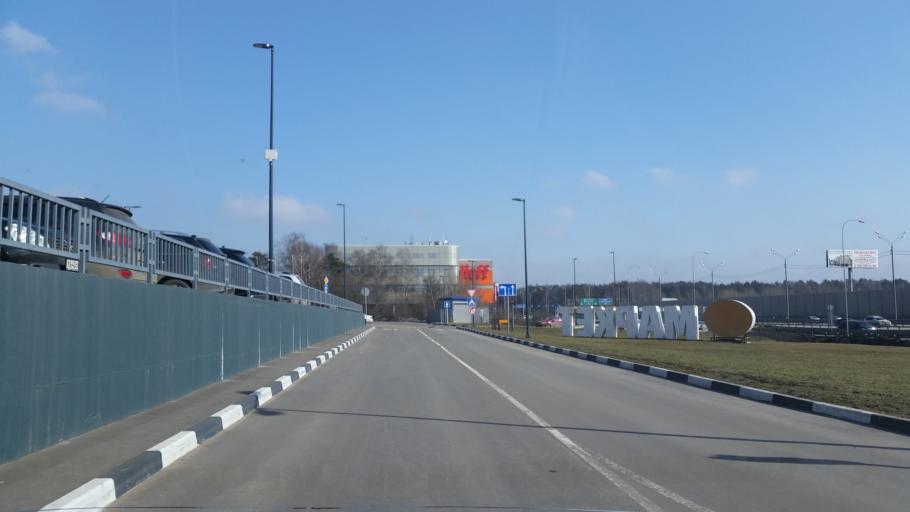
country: RU
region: Moskovskaya
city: Arkhangel'skoye
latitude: 55.7987
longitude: 37.2761
